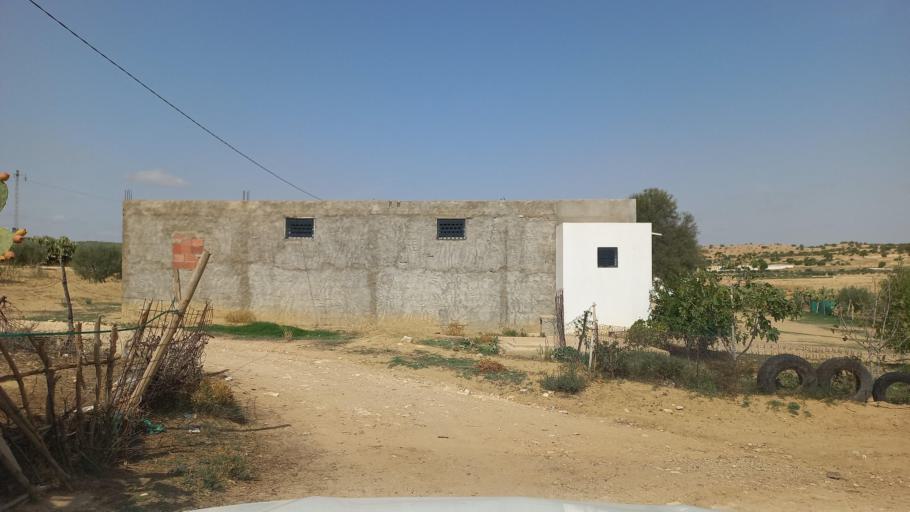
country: TN
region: Al Qasrayn
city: Sbiba
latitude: 35.3876
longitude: 8.9597
